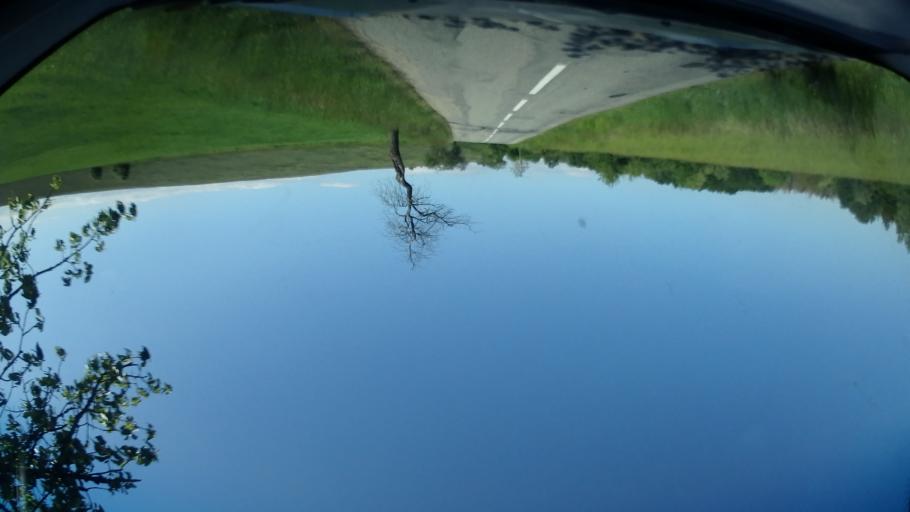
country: CZ
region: South Moravian
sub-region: Okres Blansko
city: Letovice
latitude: 49.6059
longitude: 16.6083
